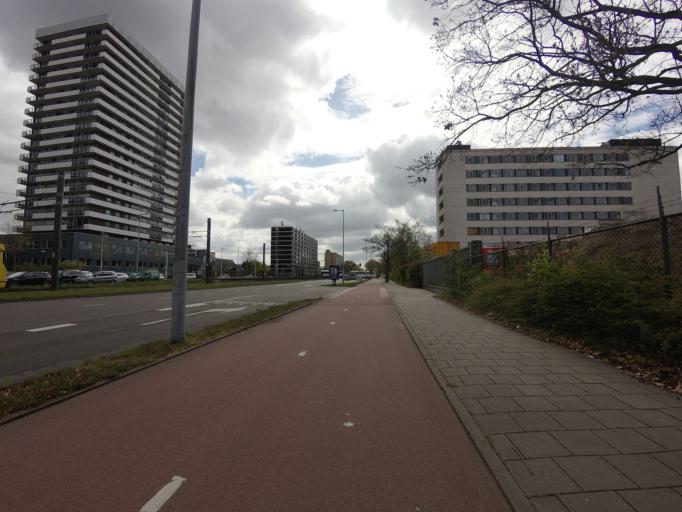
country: NL
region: Utrecht
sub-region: Gemeente Utrecht
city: Utrecht
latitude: 52.0803
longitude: 5.0911
